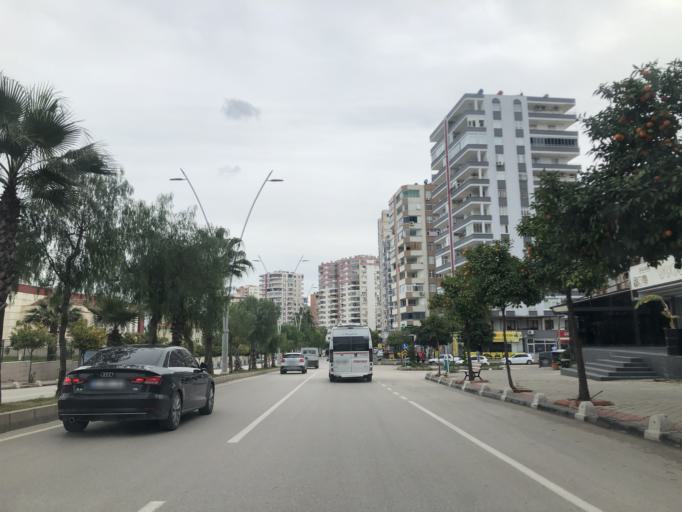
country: TR
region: Adana
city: Adana
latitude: 37.0535
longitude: 35.2900
